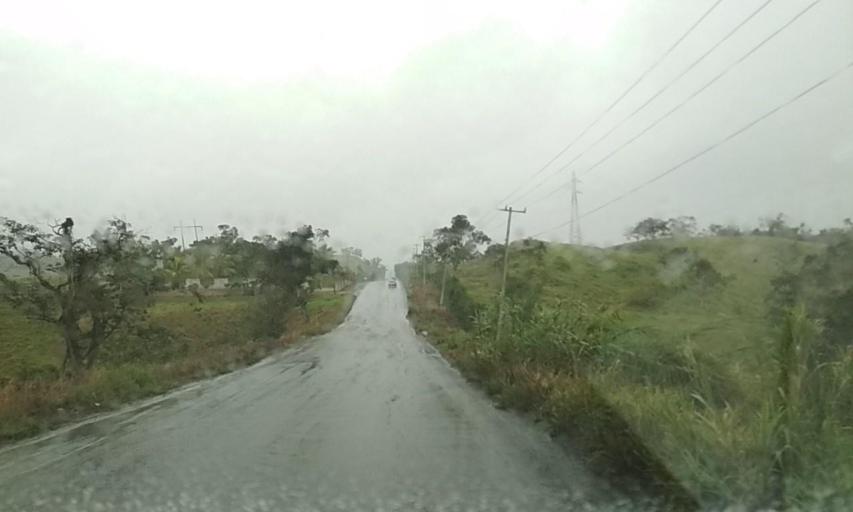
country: MX
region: Veracruz
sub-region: Papantla
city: El Chote
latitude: 20.3934
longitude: -97.3274
